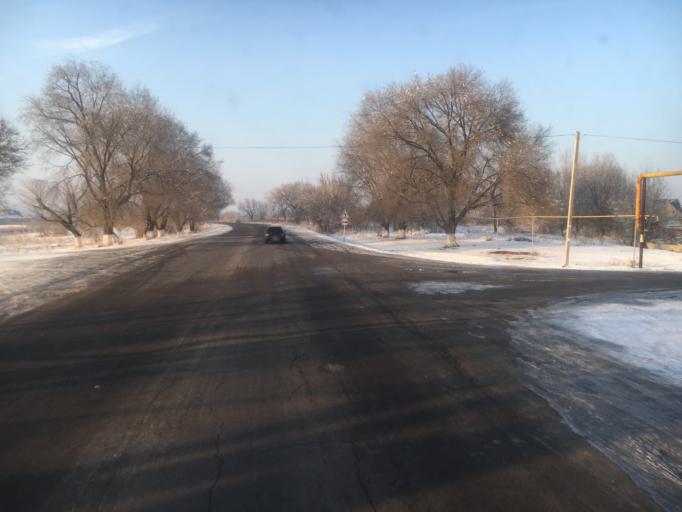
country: KZ
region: Almaty Oblysy
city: Burunday
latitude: 43.3395
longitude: 76.6590
